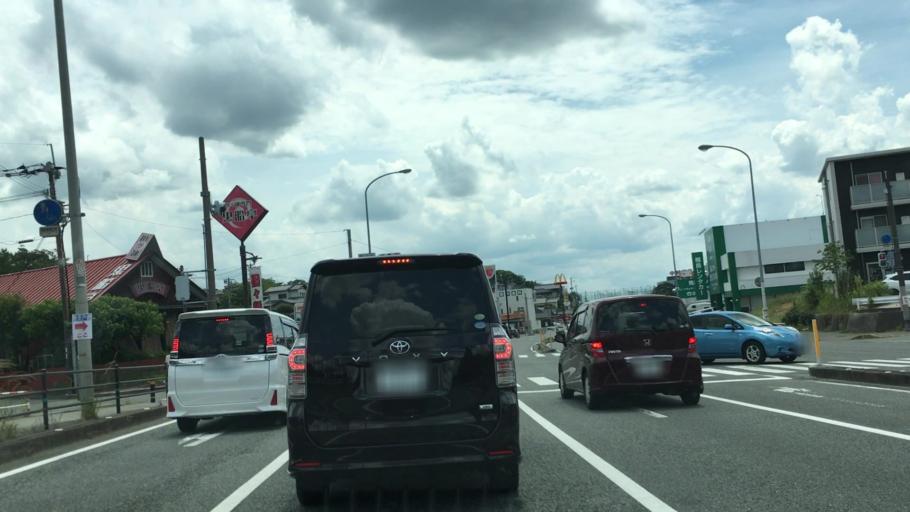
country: JP
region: Fukuoka
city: Dazaifu
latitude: 33.5036
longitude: 130.5310
